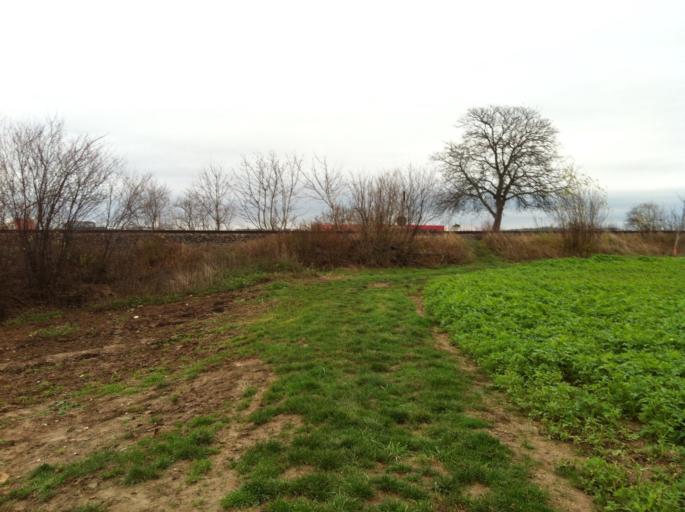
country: DE
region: Rheinland-Pfalz
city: Klein-Winternheim
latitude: 49.9848
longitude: 8.2100
